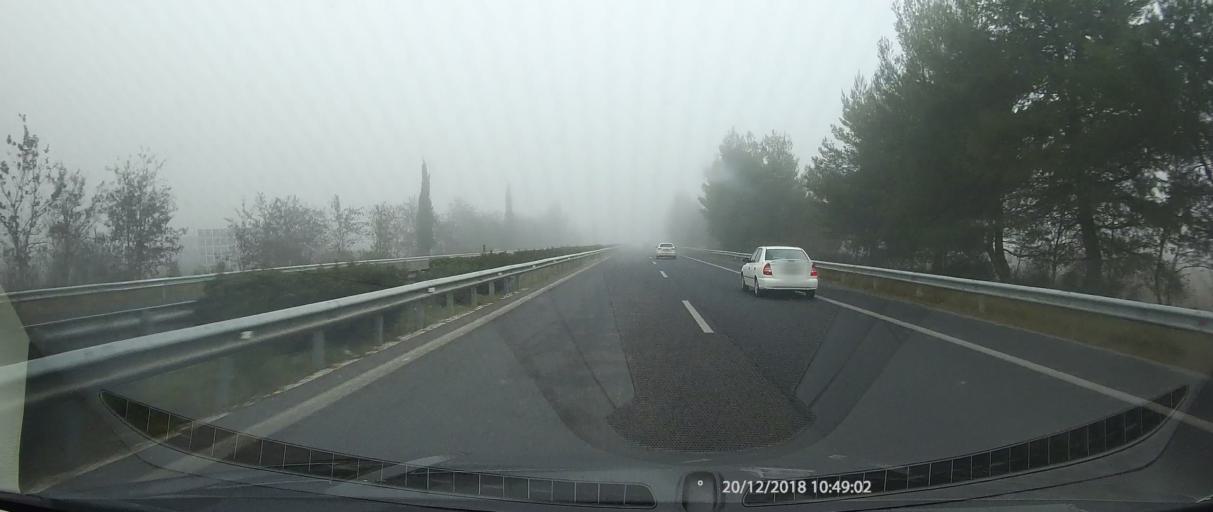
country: GR
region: Peloponnese
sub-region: Nomos Arkadias
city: Tripoli
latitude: 37.5301
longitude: 22.4114
